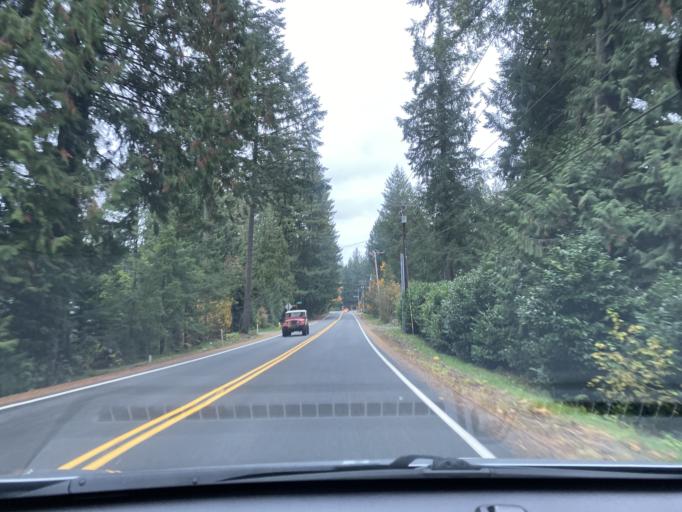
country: US
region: Washington
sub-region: King County
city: Lake Morton-Berrydale
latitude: 47.3009
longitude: -122.0903
